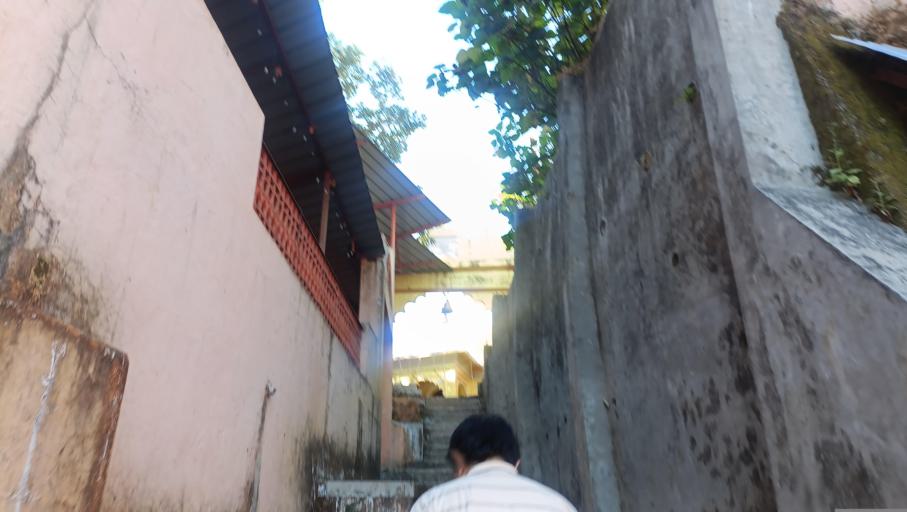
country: IN
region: Maharashtra
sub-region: Nashik Division
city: Trimbak
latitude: 19.9390
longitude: 73.5283
